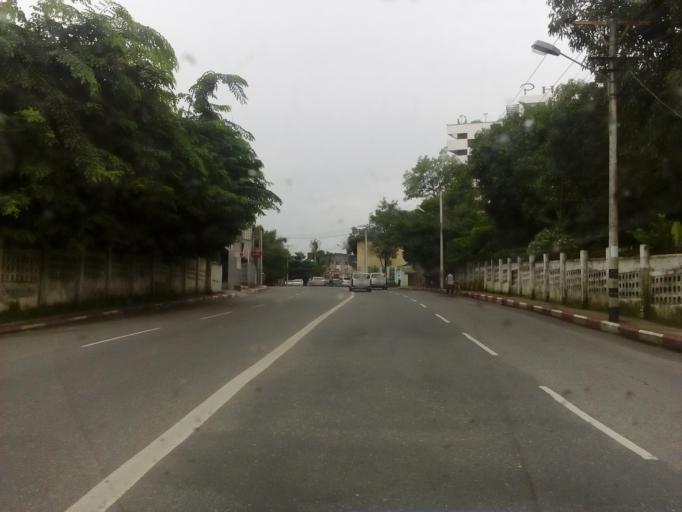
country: MM
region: Yangon
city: Yangon
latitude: 16.8510
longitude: 96.1526
